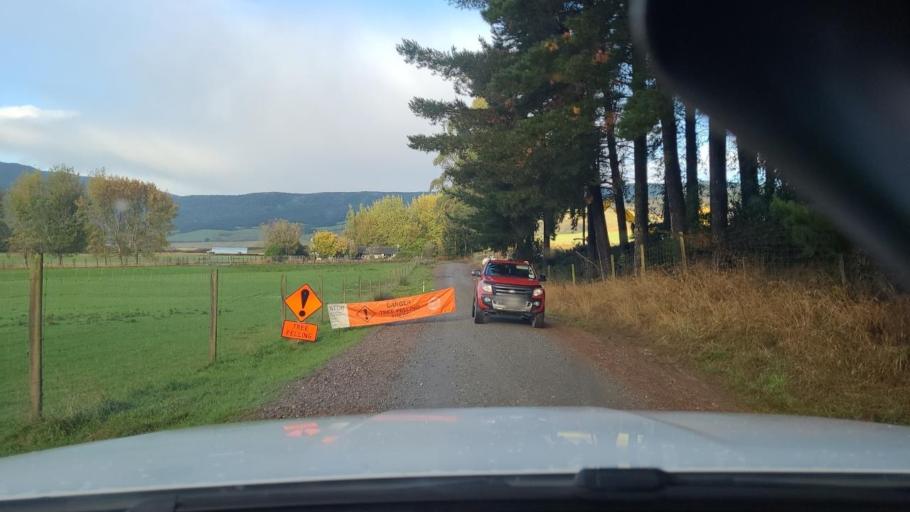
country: NZ
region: Southland
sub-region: Southland District
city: Te Anau
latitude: -45.8125
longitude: 167.6305
